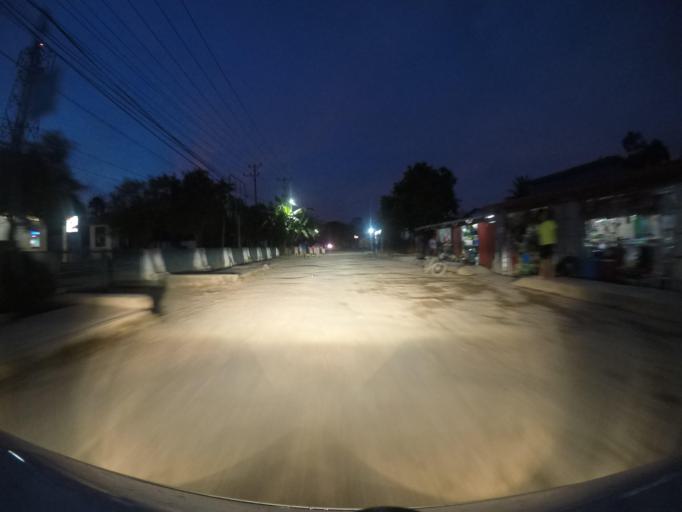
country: TL
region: Viqueque
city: Viqueque
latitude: -8.8596
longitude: 126.3648
